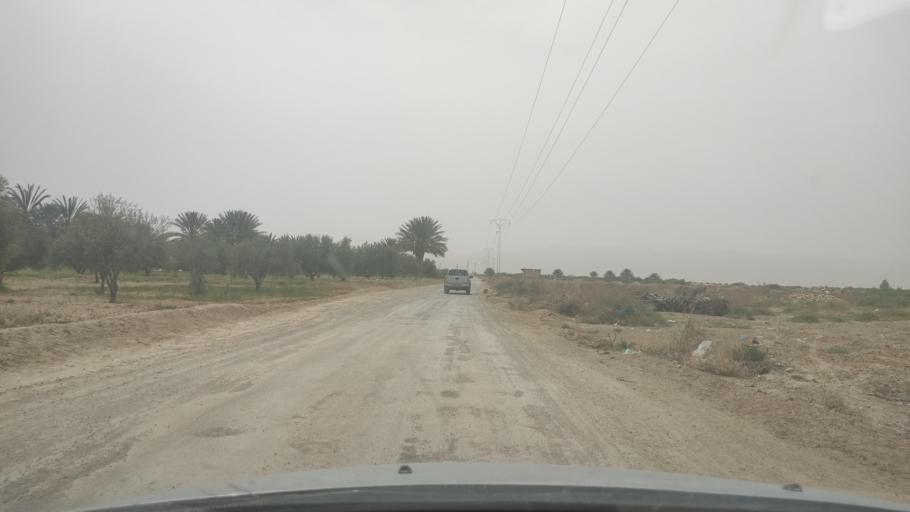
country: TN
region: Gafsa
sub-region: Gafsa Municipality
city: Gafsa
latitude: 34.3209
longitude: 8.9549
